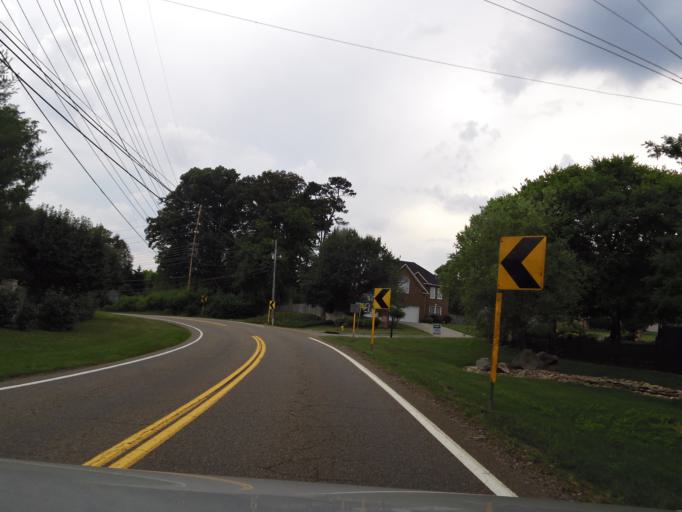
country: US
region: Tennessee
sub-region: Knox County
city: Farragut
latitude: 35.8628
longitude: -84.1158
